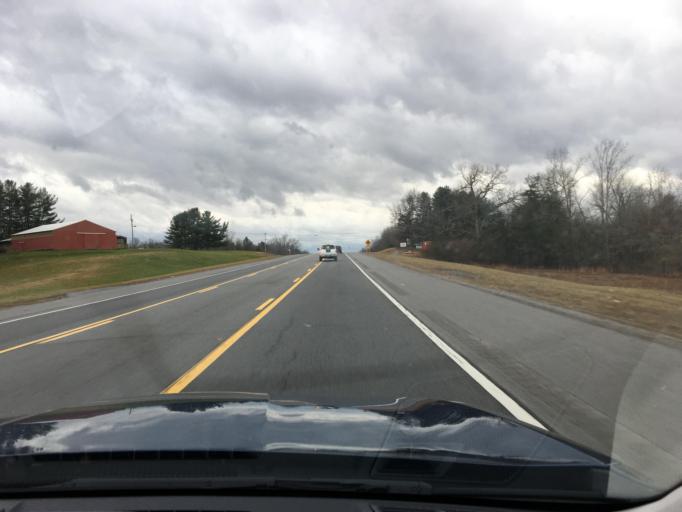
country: US
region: Tennessee
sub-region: Cumberland County
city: Crossville
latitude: 35.9515
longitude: -84.9864
